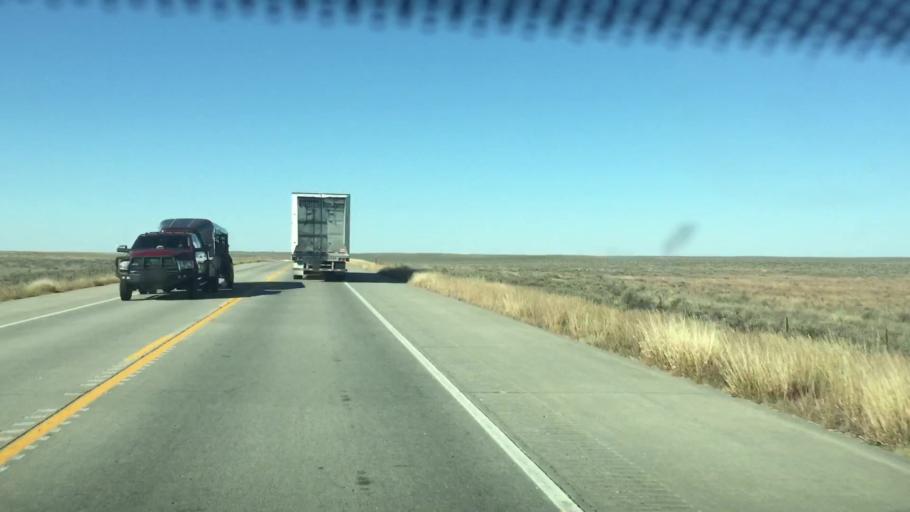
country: US
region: Colorado
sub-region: Kiowa County
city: Eads
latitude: 38.5572
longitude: -102.7862
